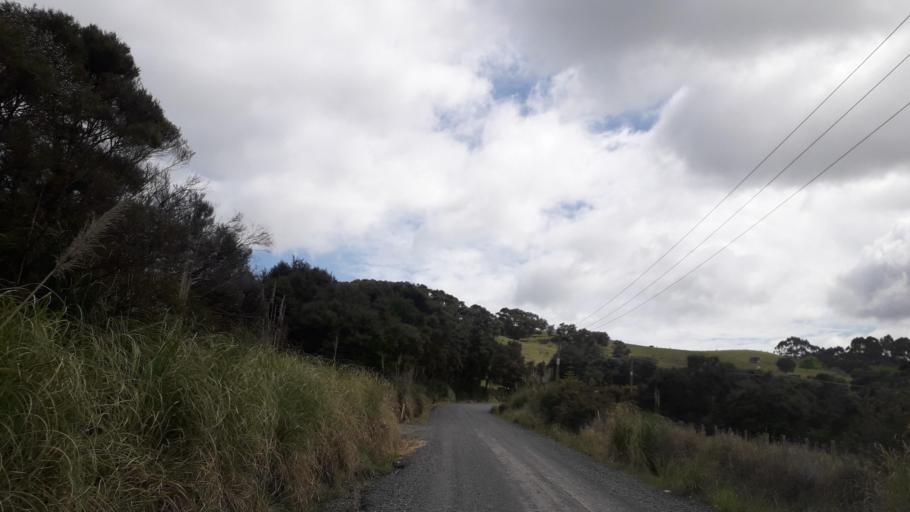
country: NZ
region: Northland
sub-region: Far North District
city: Kaitaia
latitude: -35.1602
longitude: 173.3426
